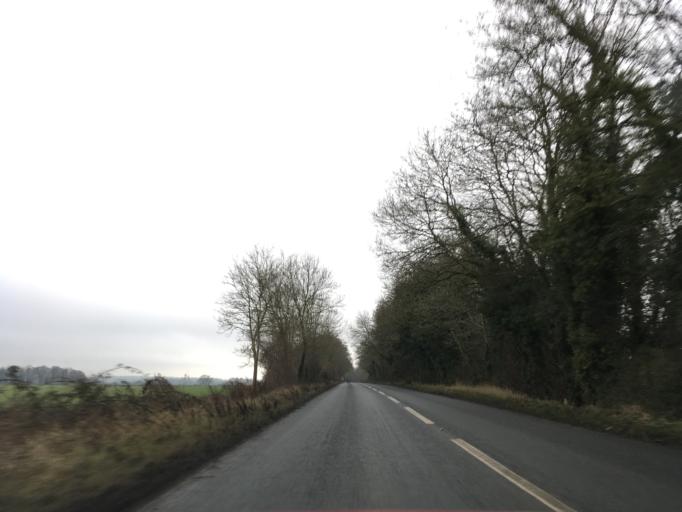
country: GB
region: England
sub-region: Gloucestershire
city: Coates
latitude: 51.6960
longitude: -2.0105
